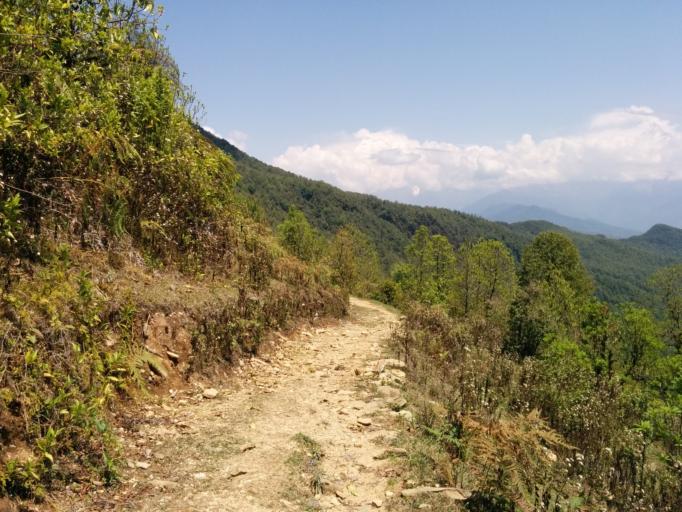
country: NP
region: Western Region
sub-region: Gandaki Zone
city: Pokhara
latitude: 28.2230
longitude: 83.8094
